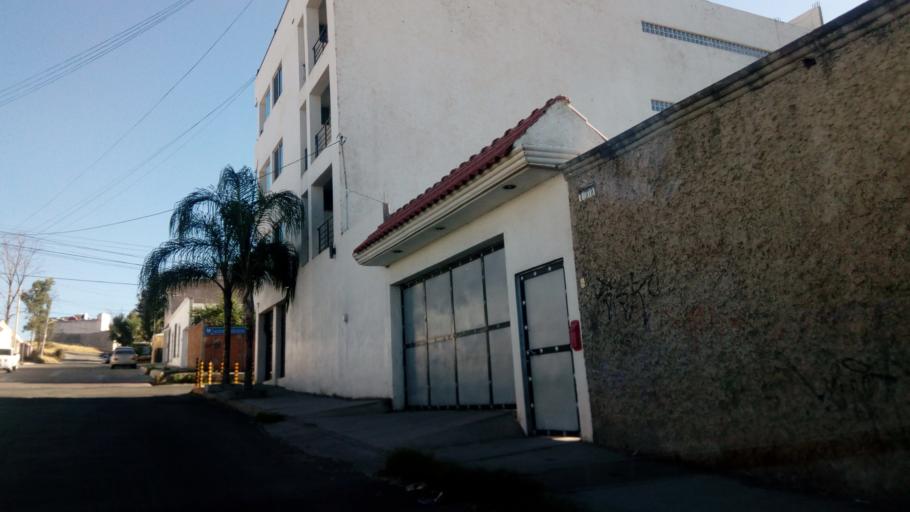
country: MX
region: Durango
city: Victoria de Durango
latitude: 24.0224
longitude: -104.6872
